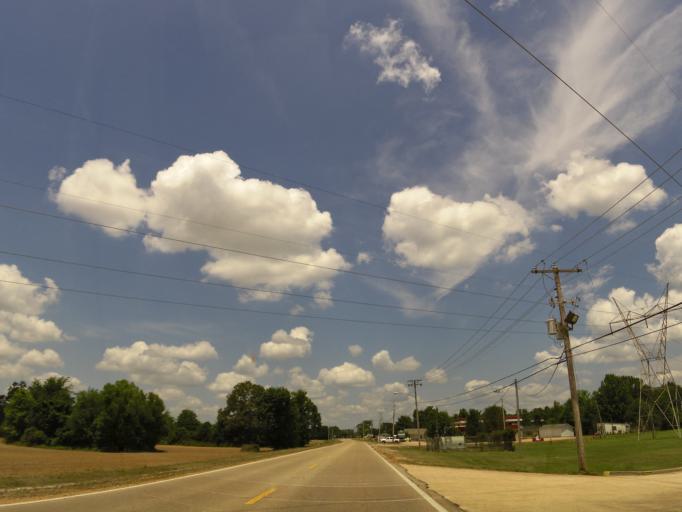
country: US
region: Mississippi
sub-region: Lee County
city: Tupelo
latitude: 34.2740
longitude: -88.6806
